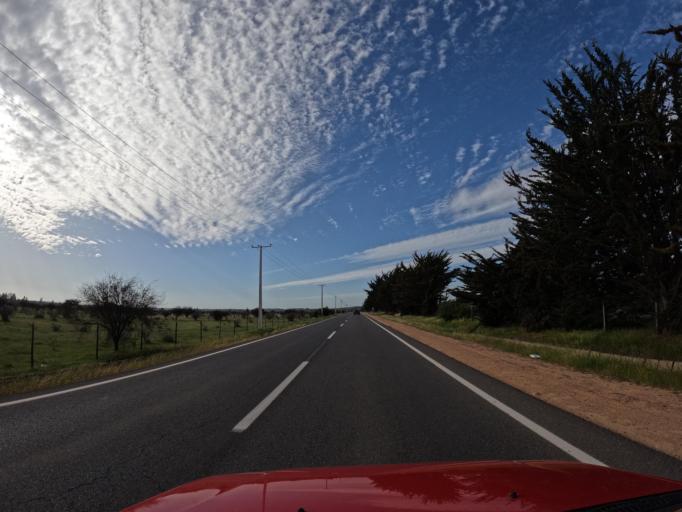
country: CL
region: Valparaiso
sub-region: San Antonio Province
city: San Antonio
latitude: -34.1555
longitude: -71.7327
